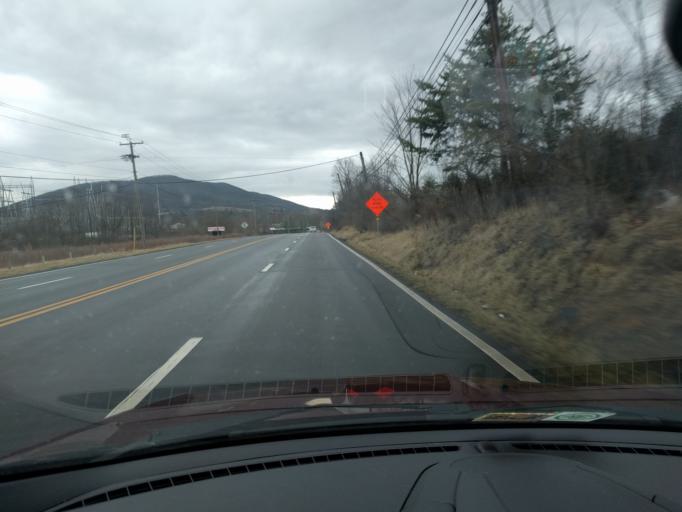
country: US
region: Virginia
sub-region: Botetourt County
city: Cloverdale
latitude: 37.3793
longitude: -79.9033
